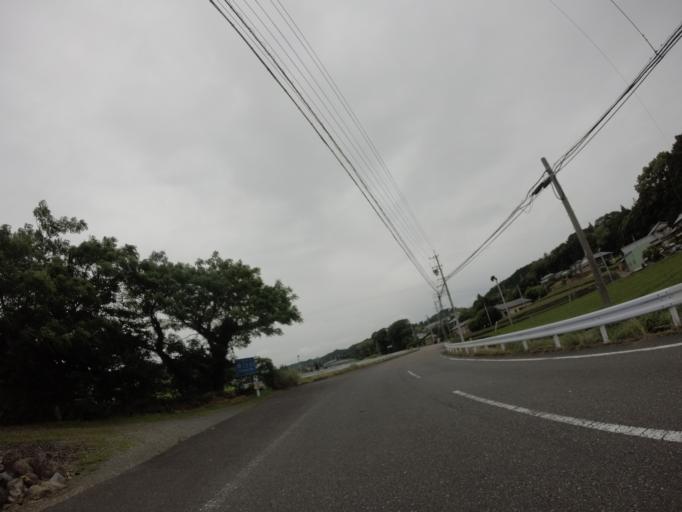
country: JP
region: Shizuoka
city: Shimada
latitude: 34.8036
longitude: 138.1876
